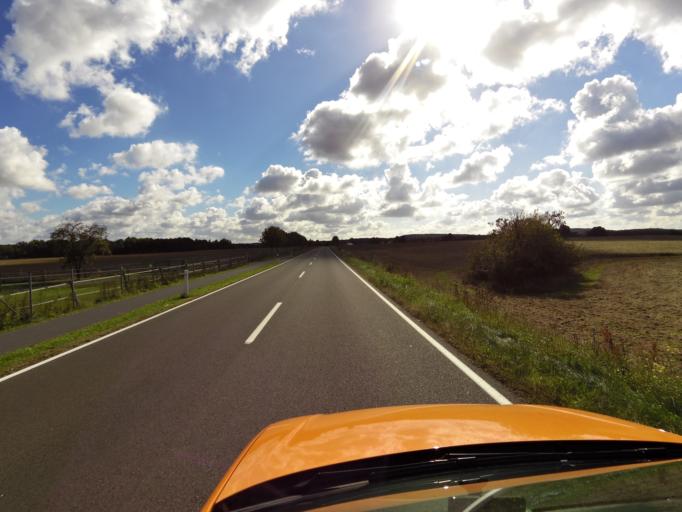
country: DE
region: Brandenburg
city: Michendorf
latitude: 52.2894
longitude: 13.0553
